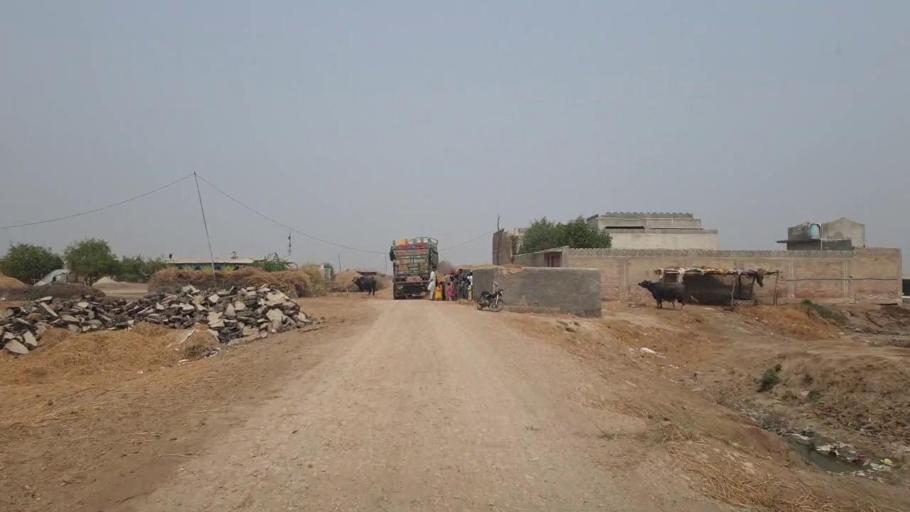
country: PK
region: Sindh
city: Kario
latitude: 24.6592
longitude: 68.6397
